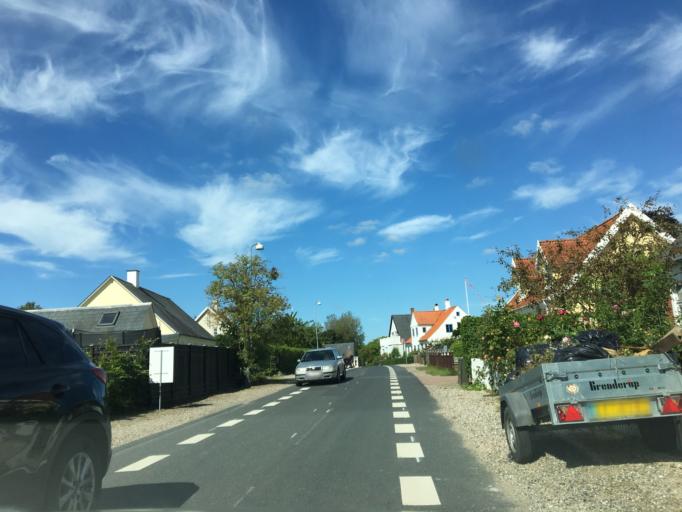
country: DK
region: South Denmark
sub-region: Svendborg Kommune
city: Thuro By
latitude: 55.0467
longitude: 10.6731
